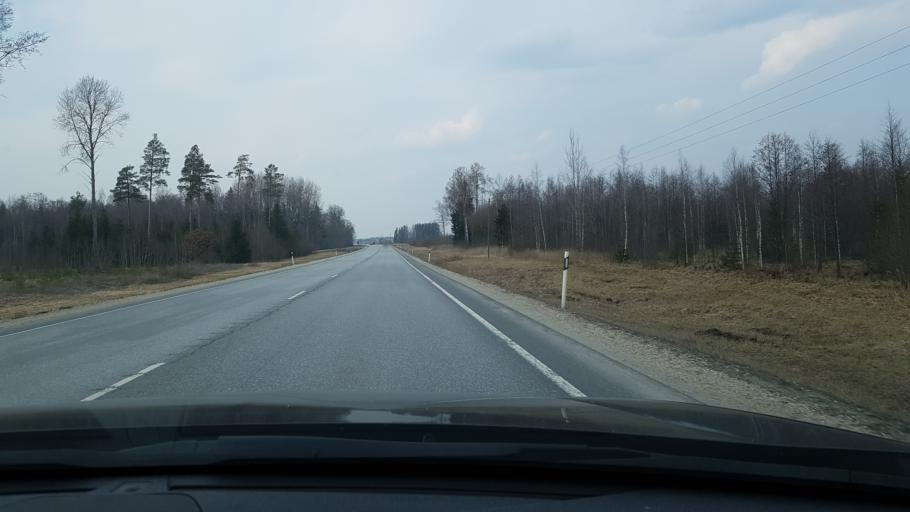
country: EE
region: Tartu
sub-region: Puhja vald
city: Puhja
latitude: 58.5432
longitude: 26.3034
